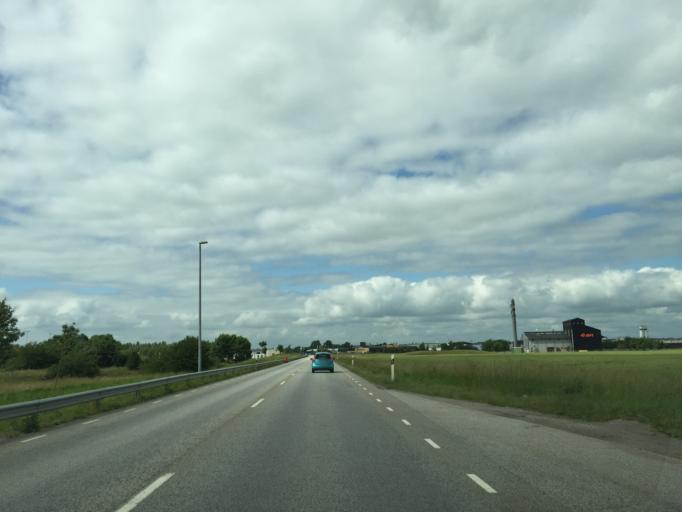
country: SE
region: Skane
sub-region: Staffanstorps Kommun
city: Staffanstorp
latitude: 55.6456
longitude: 13.2306
